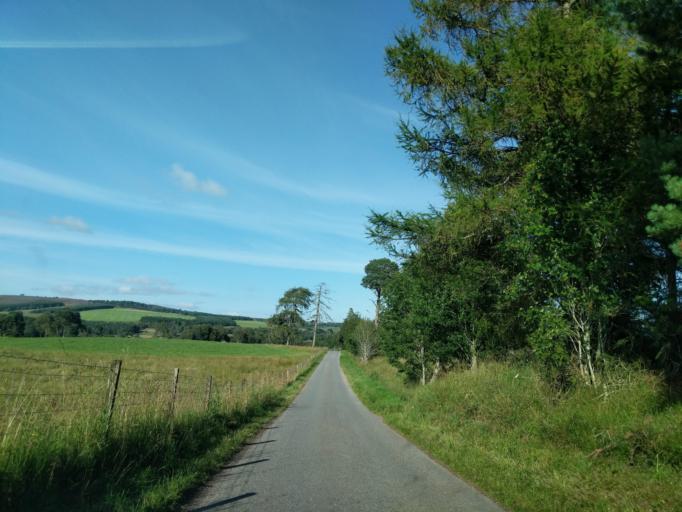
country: GB
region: Scotland
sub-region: Highland
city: Grantown on Spey
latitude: 57.2973
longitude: -3.7088
